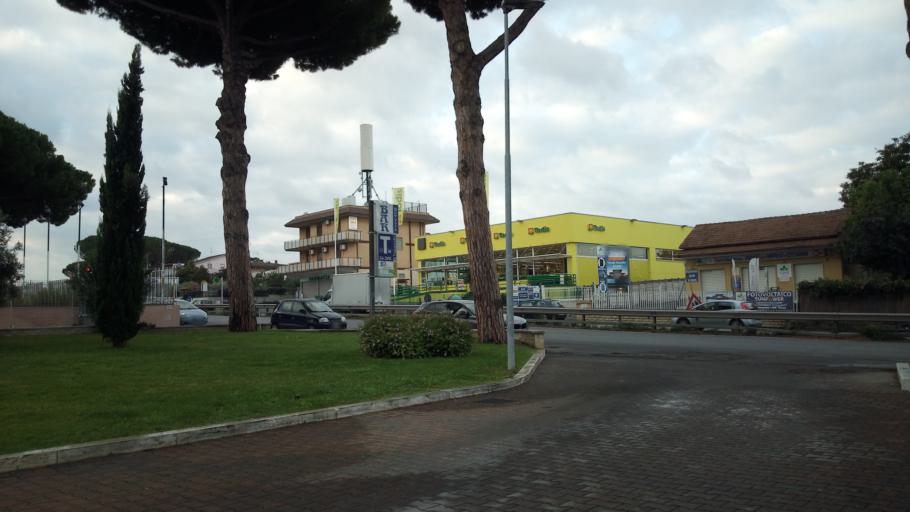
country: IT
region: Latium
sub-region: Citta metropolitana di Roma Capitale
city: Ciampino
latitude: 41.8110
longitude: 12.6256
